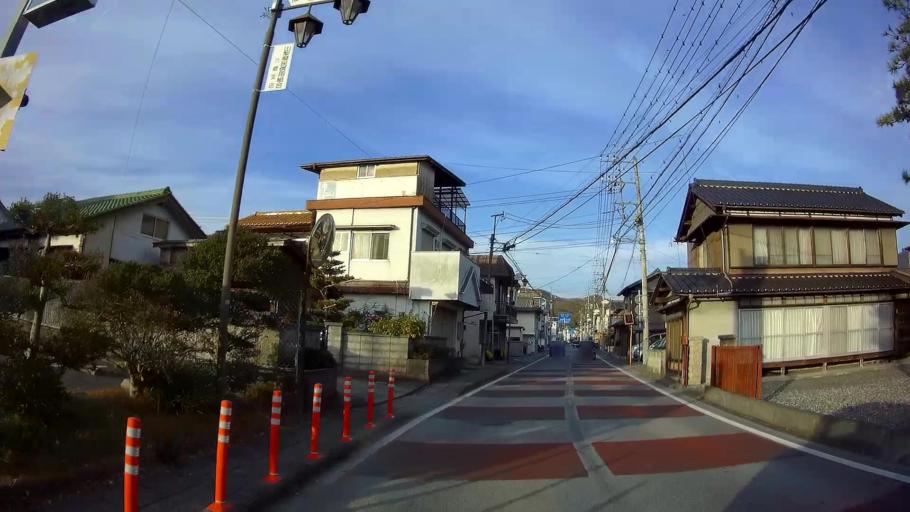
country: JP
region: Yamanashi
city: Ryuo
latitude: 35.4914
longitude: 138.4599
